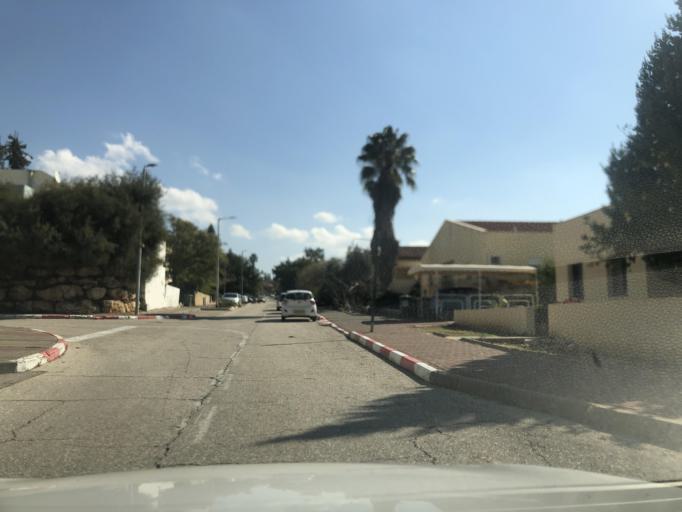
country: PS
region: West Bank
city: Azun Atme
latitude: 32.1108
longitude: 35.0305
